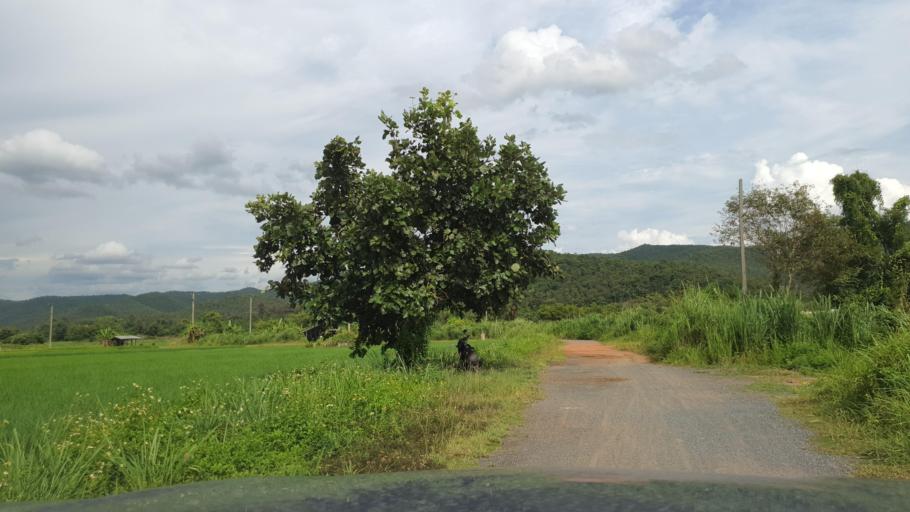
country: TH
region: Chiang Mai
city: Mae On
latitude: 18.7817
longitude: 99.1853
